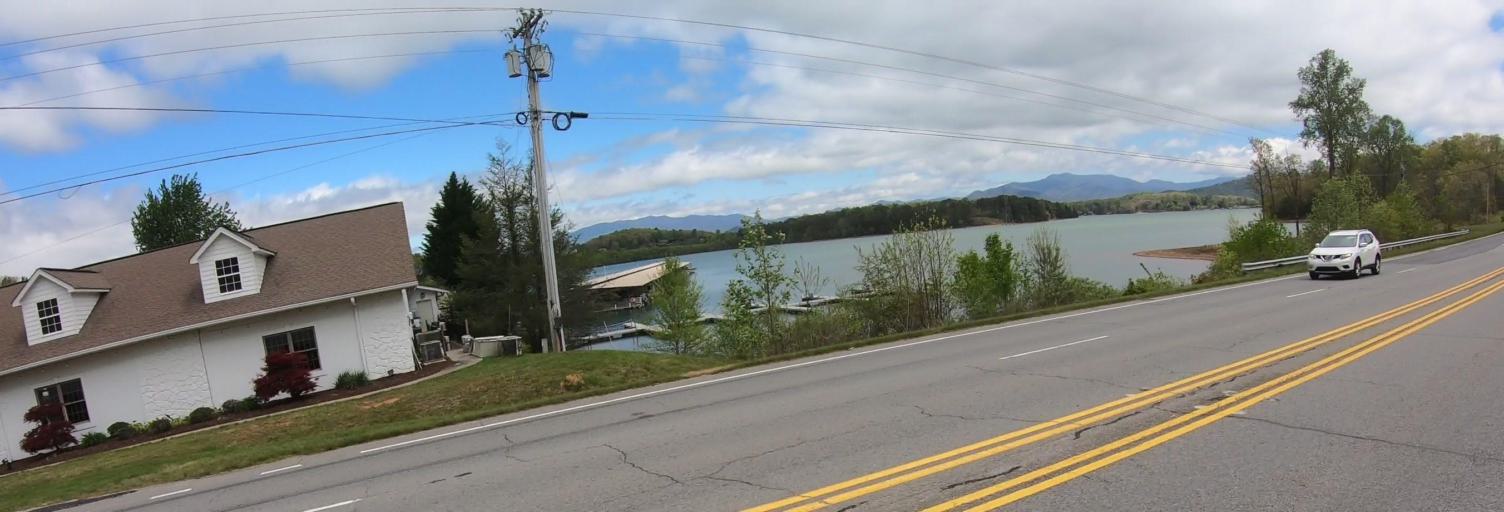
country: US
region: Georgia
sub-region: Towns County
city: Hiawassee
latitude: 34.9687
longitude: -83.8145
